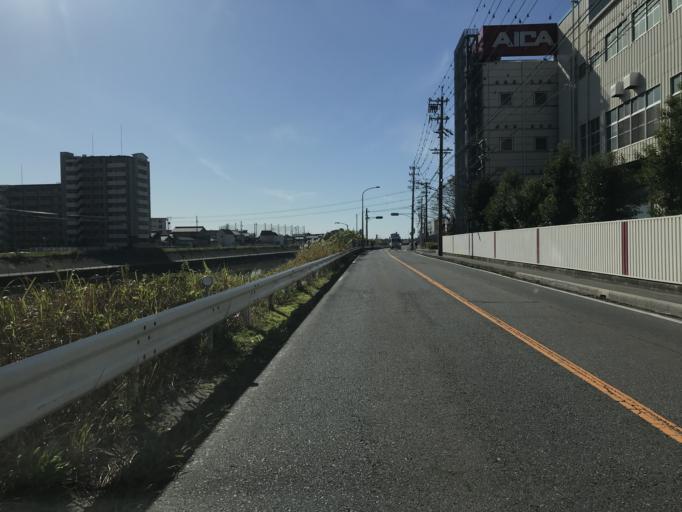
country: JP
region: Aichi
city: Nagoya-shi
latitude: 35.1900
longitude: 136.8478
